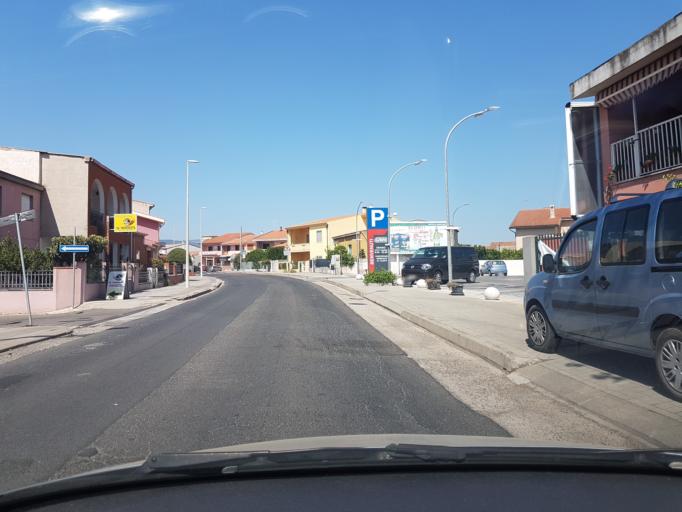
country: IT
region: Sardinia
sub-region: Provincia di Oristano
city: Riola Sardo
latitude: 39.9898
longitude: 8.5415
